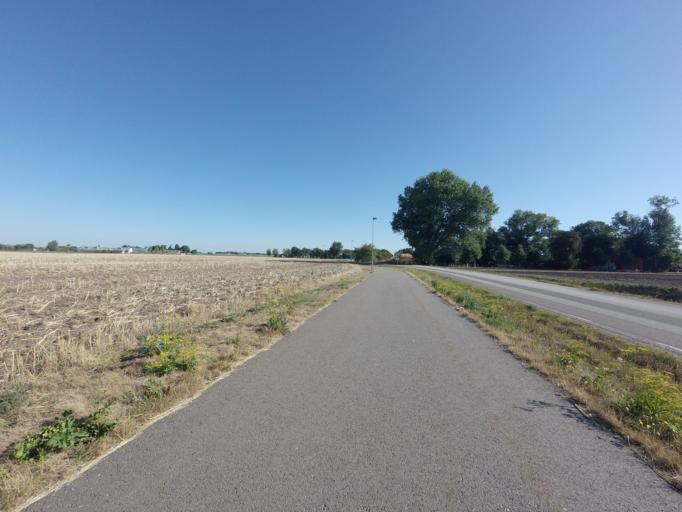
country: SE
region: Skane
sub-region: Trelleborgs Kommun
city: Skare
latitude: 55.4016
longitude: 13.0906
